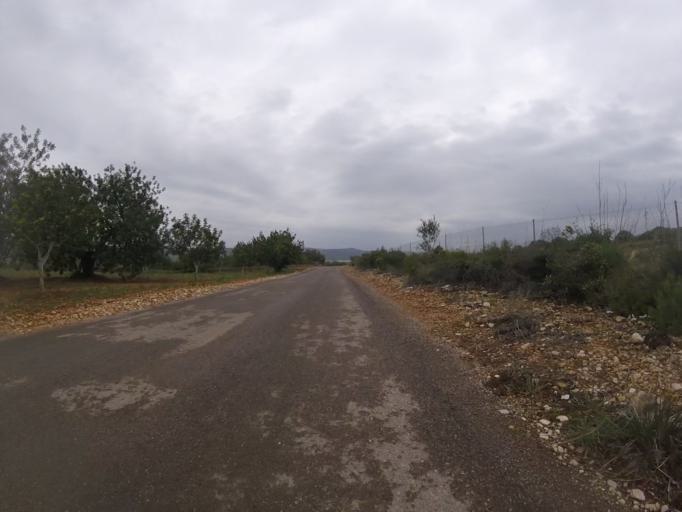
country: ES
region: Valencia
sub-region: Provincia de Castello
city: Alcala de Xivert
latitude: 40.2819
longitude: 0.2287
